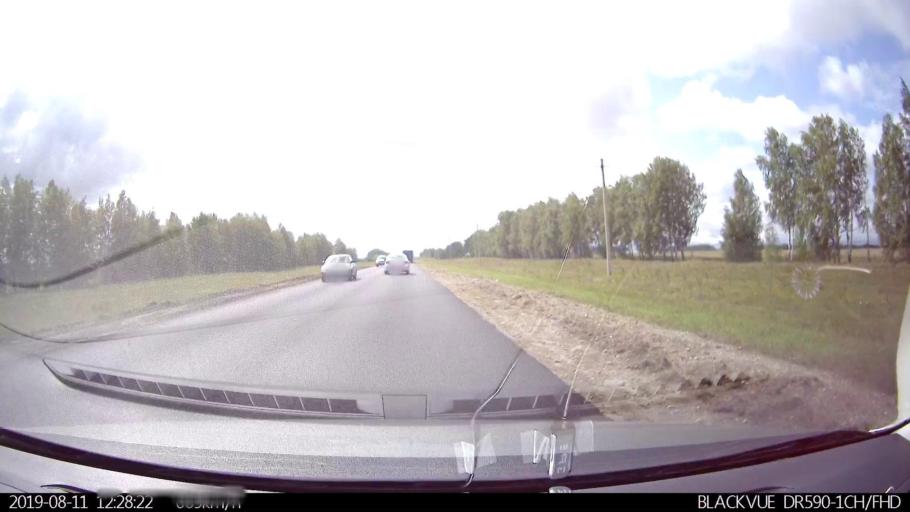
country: RU
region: Ulyanovsk
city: Ignatovka
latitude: 53.8446
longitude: 47.9115
